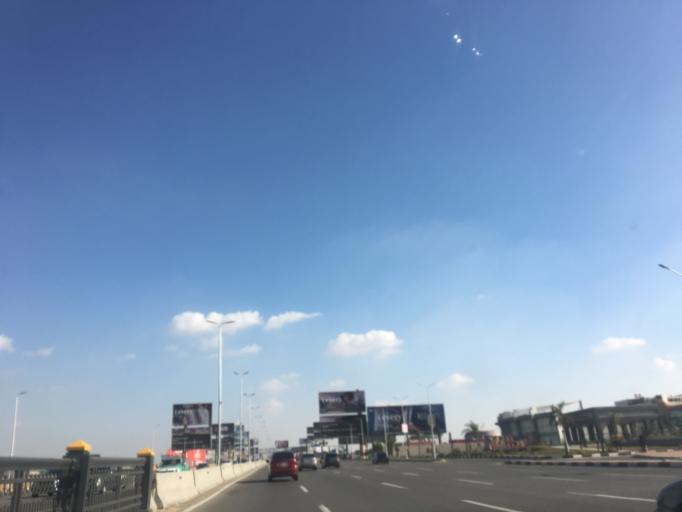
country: EG
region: Muhafazat al Qahirah
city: Cairo
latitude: 30.0181
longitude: 31.3873
